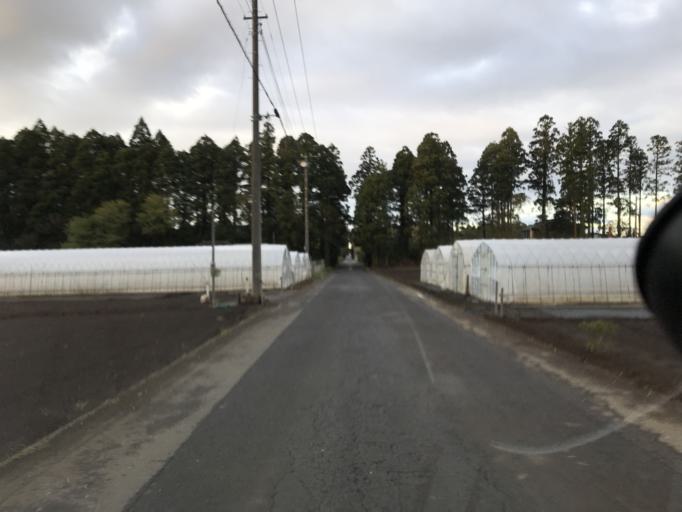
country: JP
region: Chiba
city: Sawara
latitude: 35.7931
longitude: 140.4489
